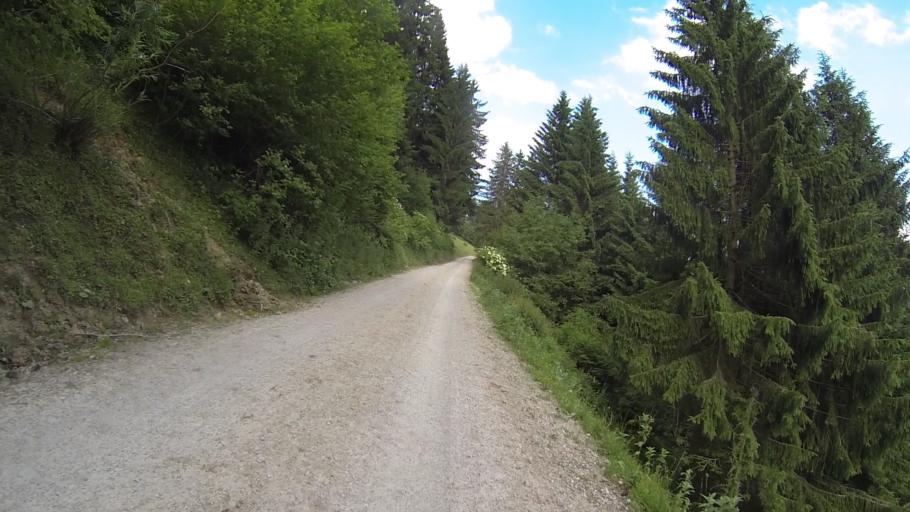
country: AT
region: Tyrol
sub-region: Politischer Bezirk Reutte
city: Jungholz
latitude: 47.5720
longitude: 10.4777
